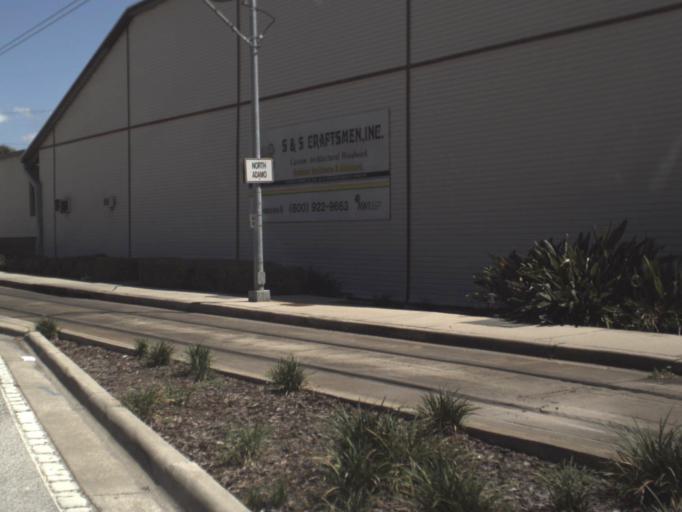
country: US
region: Florida
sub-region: Hillsborough County
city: Tampa
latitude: 27.9561
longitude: -82.4455
